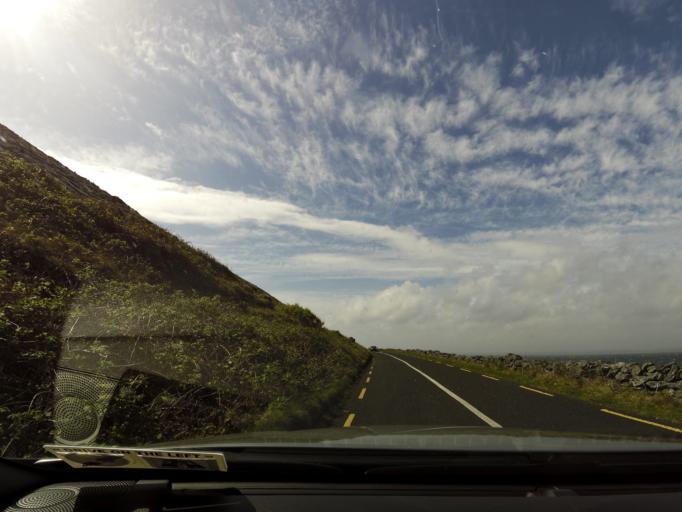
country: IE
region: Connaught
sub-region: County Galway
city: Bearna
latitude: 53.1520
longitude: -9.2576
